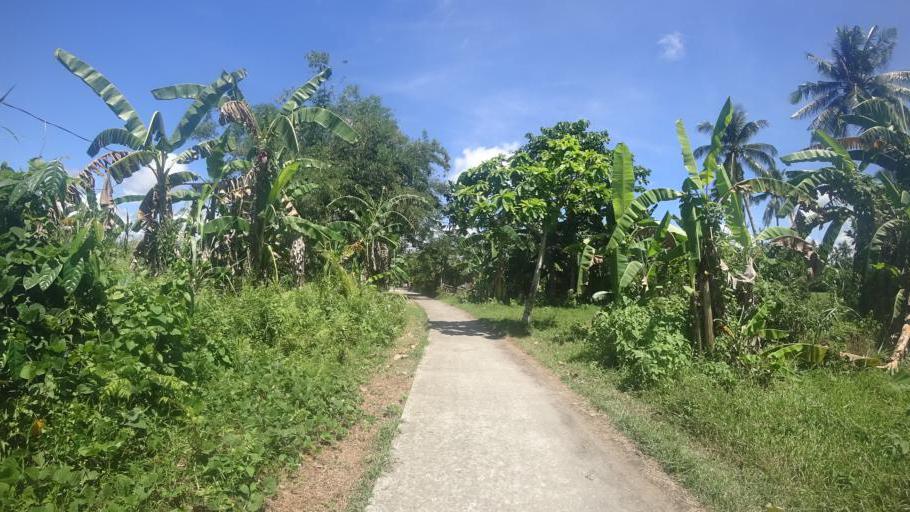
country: PH
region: Eastern Visayas
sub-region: Province of Leyte
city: Liberty
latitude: 10.8833
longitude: 124.9839
